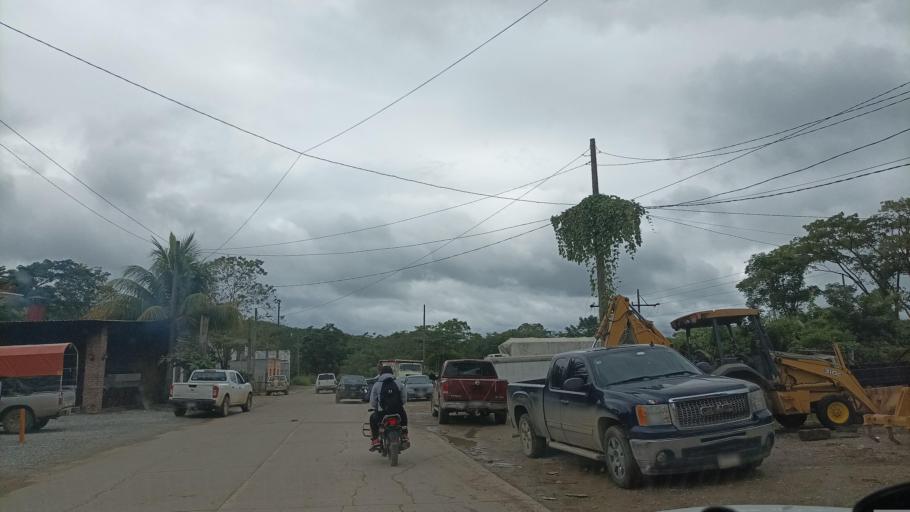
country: MX
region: Veracruz
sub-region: Uxpanapa
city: Poblado 10
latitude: 17.2778
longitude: -94.4578
